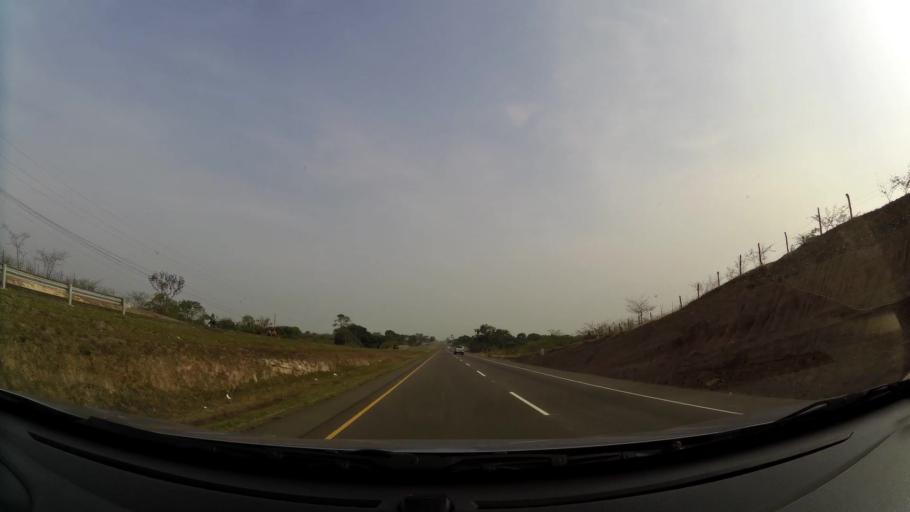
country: HN
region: La Paz
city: Yarumela
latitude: 14.3553
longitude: -87.5986
